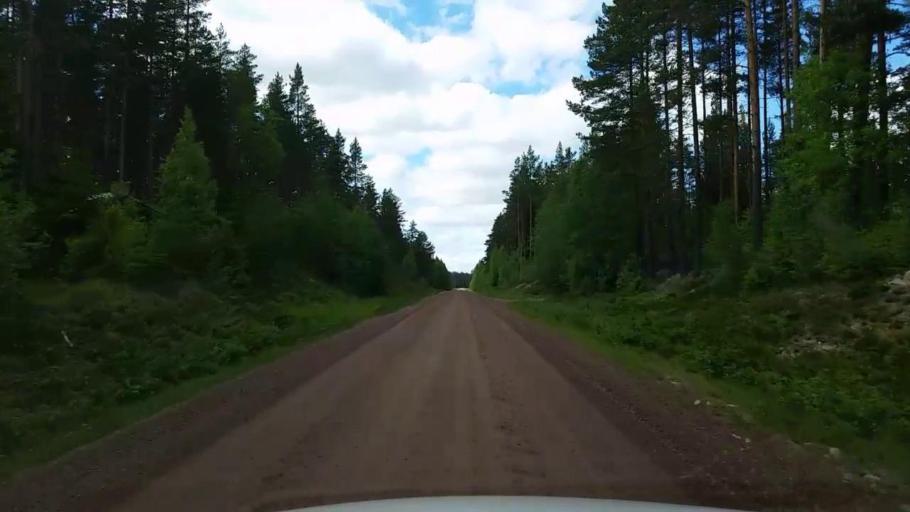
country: SE
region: Gaevleborg
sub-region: Ovanakers Kommun
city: Alfta
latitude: 61.4746
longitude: 16.0096
